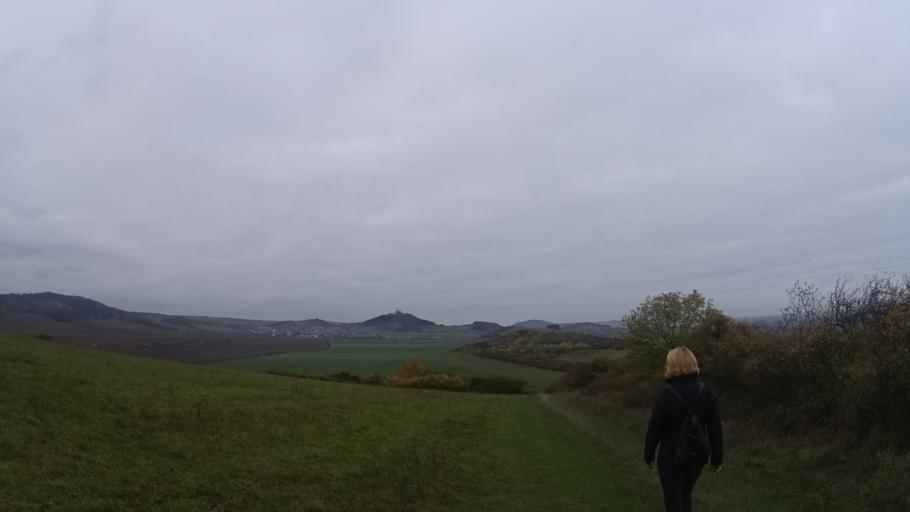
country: DE
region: Thuringia
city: Arnstadt
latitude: 50.8500
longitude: 10.9217
